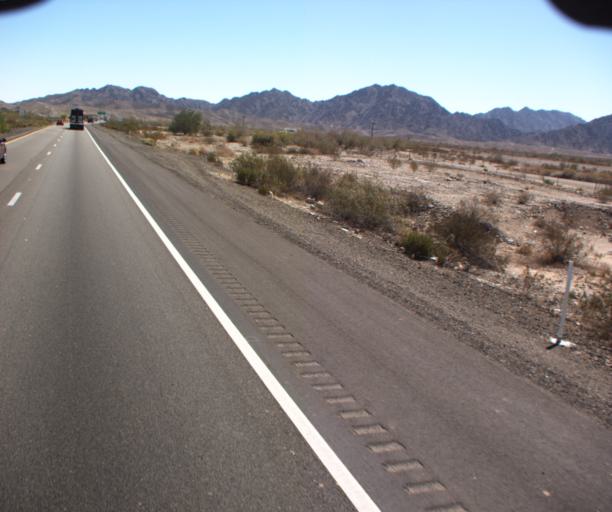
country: US
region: Arizona
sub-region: Yuma County
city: Fortuna Foothills
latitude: 32.6608
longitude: -114.3739
